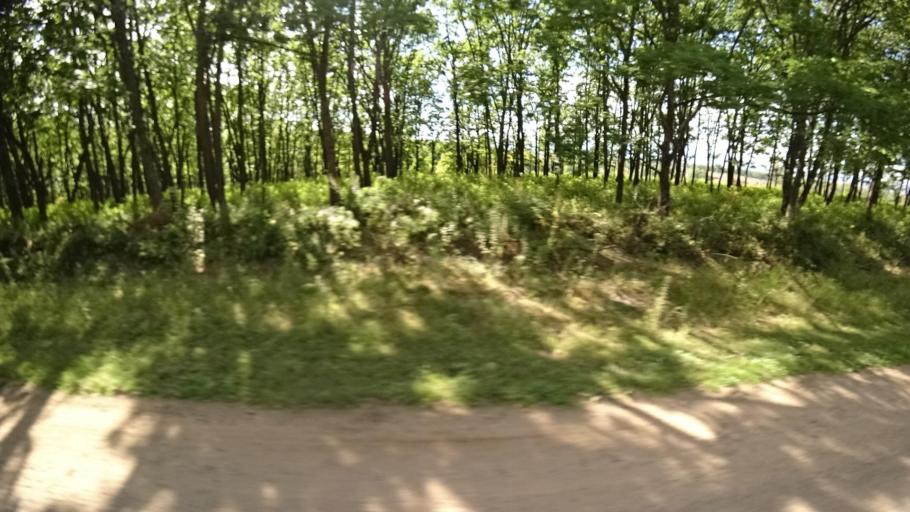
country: RU
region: Primorskiy
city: Yakovlevka
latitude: 44.4105
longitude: 133.5692
